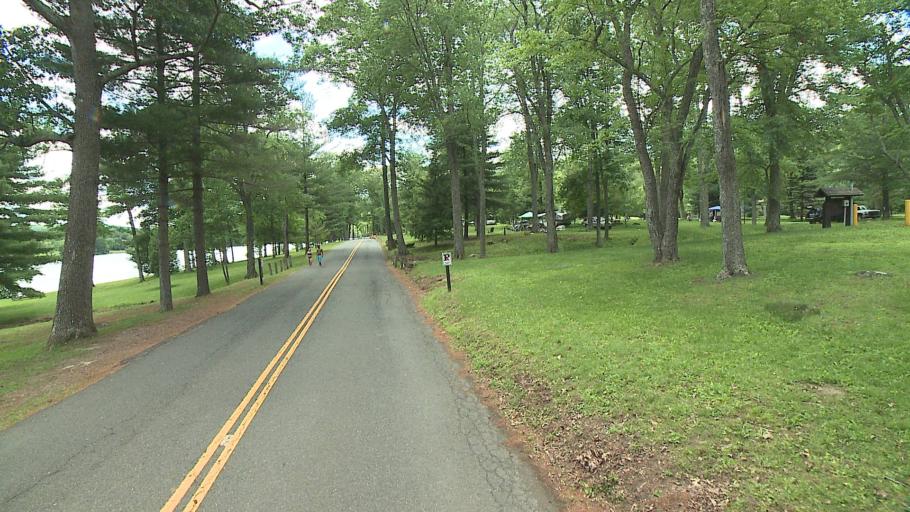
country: US
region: Connecticut
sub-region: Litchfield County
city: New Preston
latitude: 41.7068
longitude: -73.3828
